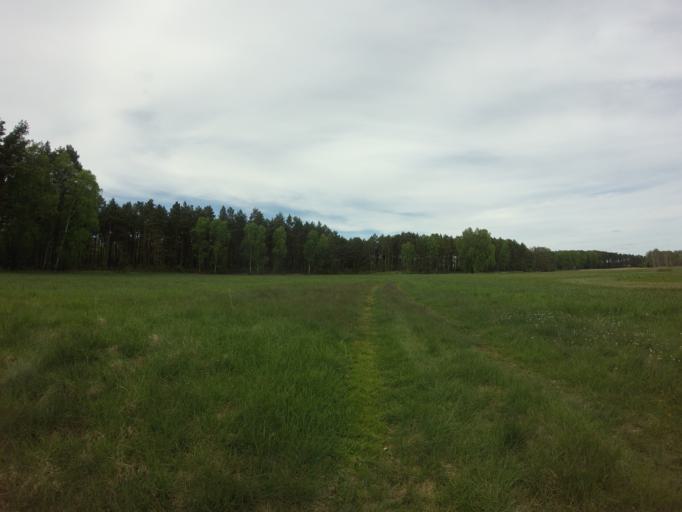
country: PL
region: West Pomeranian Voivodeship
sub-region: Powiat choszczenski
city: Drawno
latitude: 53.1632
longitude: 15.6662
